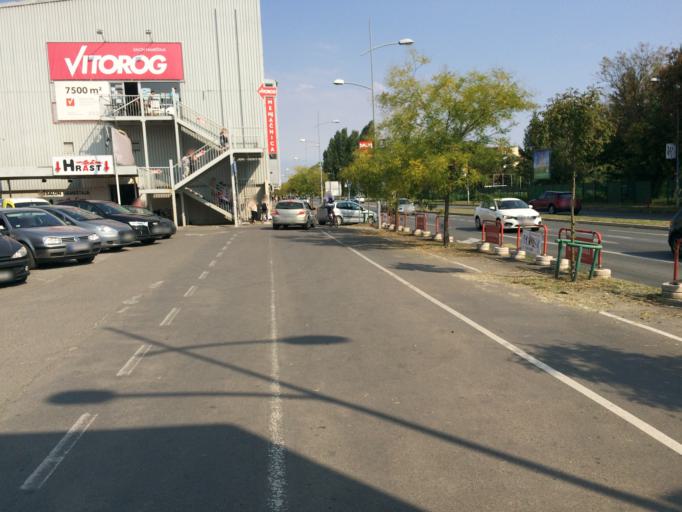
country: RS
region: Autonomna Pokrajina Vojvodina
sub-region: Juznobacki Okrug
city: Novi Sad
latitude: 45.2545
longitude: 19.8241
